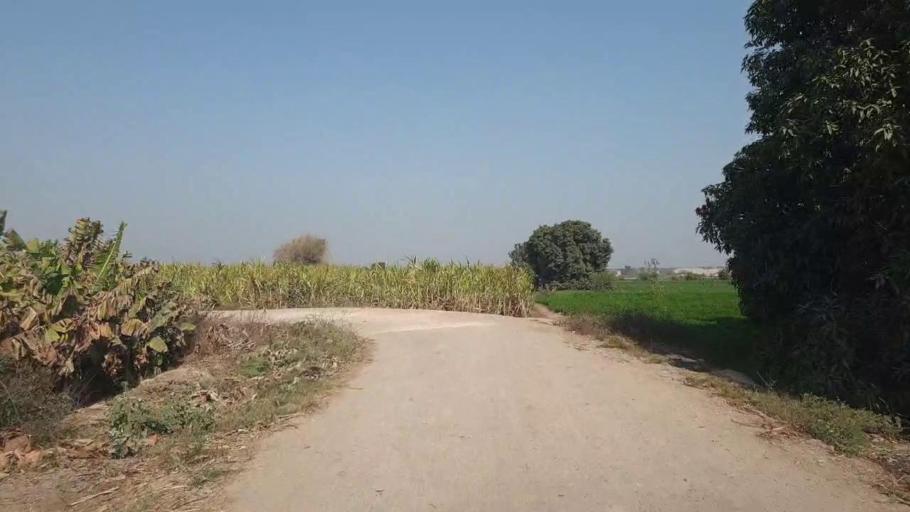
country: PK
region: Sindh
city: Tando Jam
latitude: 25.3294
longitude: 68.6007
